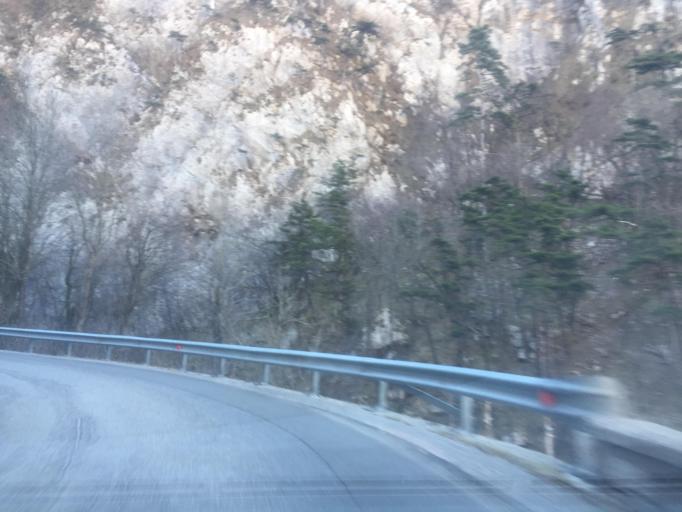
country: IT
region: Friuli Venezia Giulia
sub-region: Provincia di Udine
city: Tolmezzo
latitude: 46.4150
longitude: 13.0504
